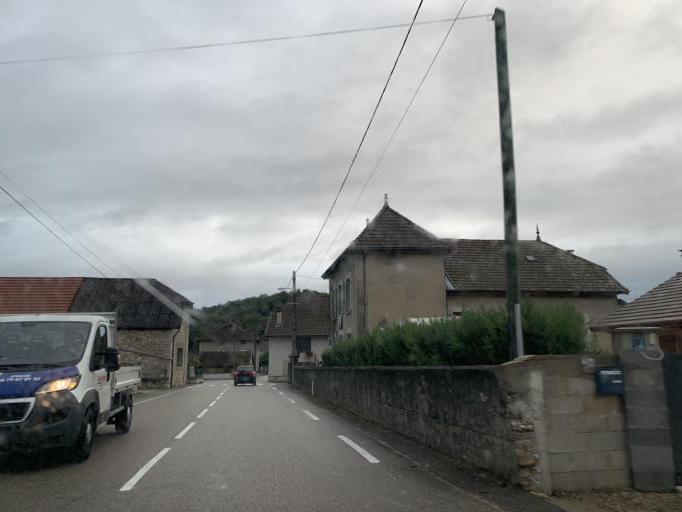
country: FR
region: Rhone-Alpes
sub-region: Departement de l'Ain
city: Belley
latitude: 45.7089
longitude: 5.6570
